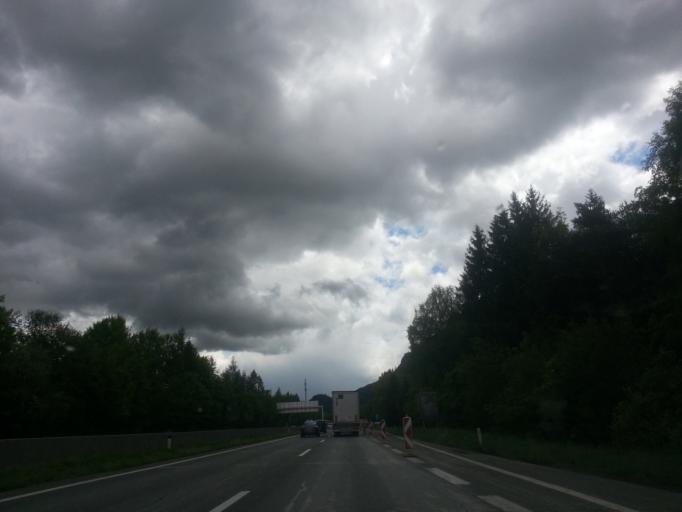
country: AT
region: Salzburg
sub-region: Politischer Bezirk Salzburg-Umgebung
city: Grodig
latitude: 47.7597
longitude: 13.0032
